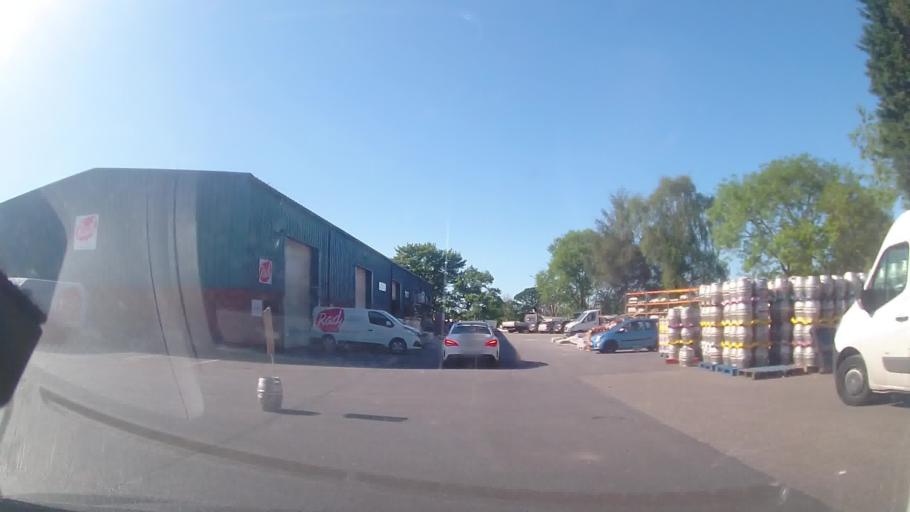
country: GB
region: England
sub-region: Shropshire
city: Astley
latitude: 52.7741
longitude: -2.7157
